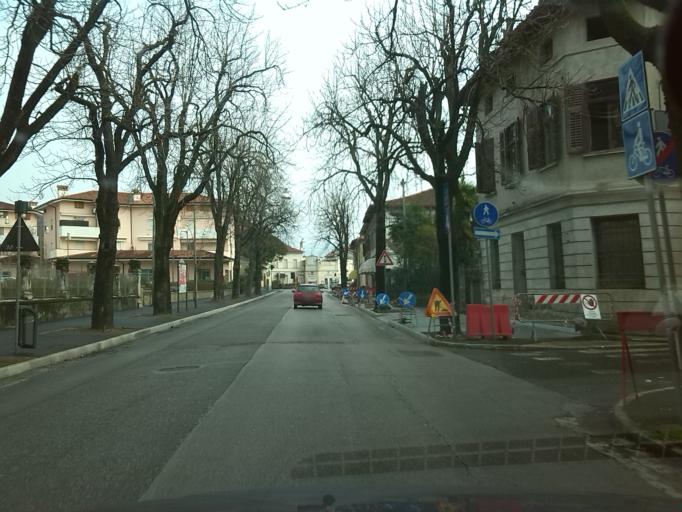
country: IT
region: Friuli Venezia Giulia
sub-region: Provincia di Gorizia
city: Mossa
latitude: 45.9359
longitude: 13.5735
